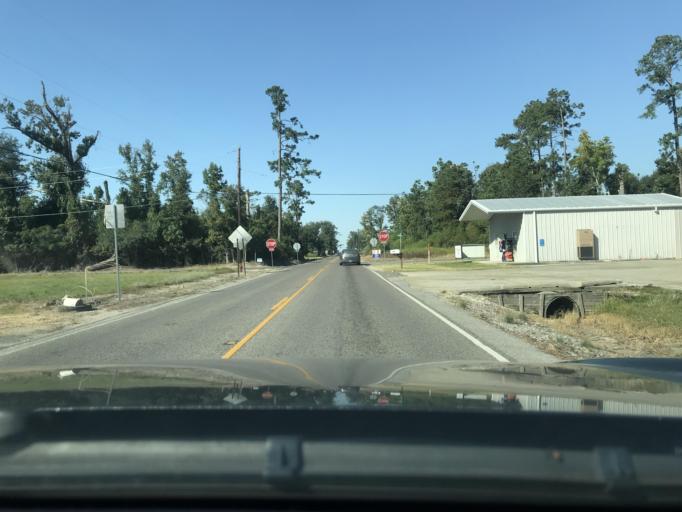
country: US
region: Louisiana
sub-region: Calcasieu Parish
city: Moss Bluff
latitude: 30.3108
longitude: -93.2001
